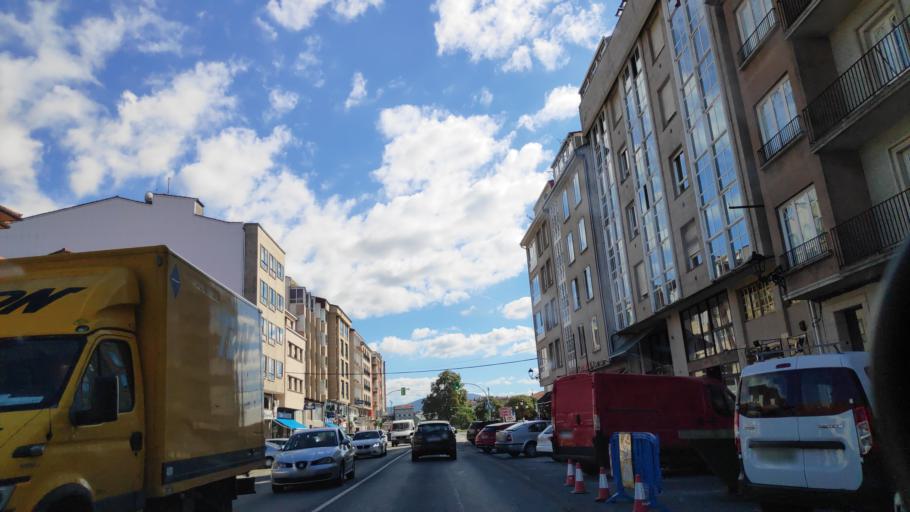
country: ES
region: Galicia
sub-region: Provincia da Coruna
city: Padron
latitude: 42.7381
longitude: -8.6594
